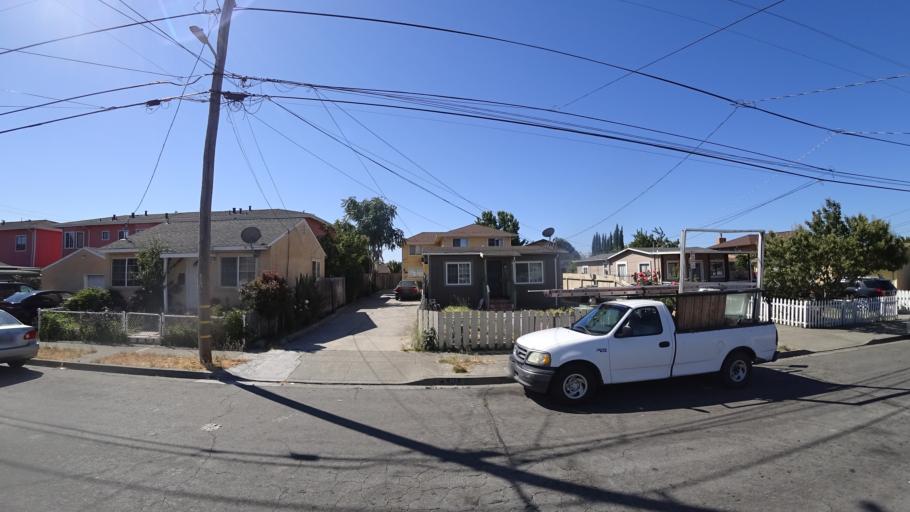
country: US
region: California
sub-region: Alameda County
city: Hayward
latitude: 37.6656
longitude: -122.0847
